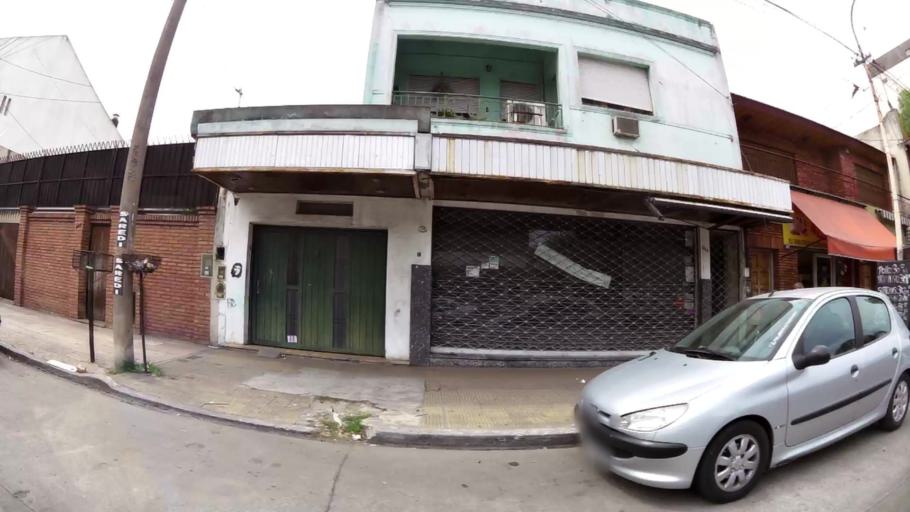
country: AR
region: Buenos Aires F.D.
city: Villa Lugano
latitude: -34.7007
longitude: -58.5098
